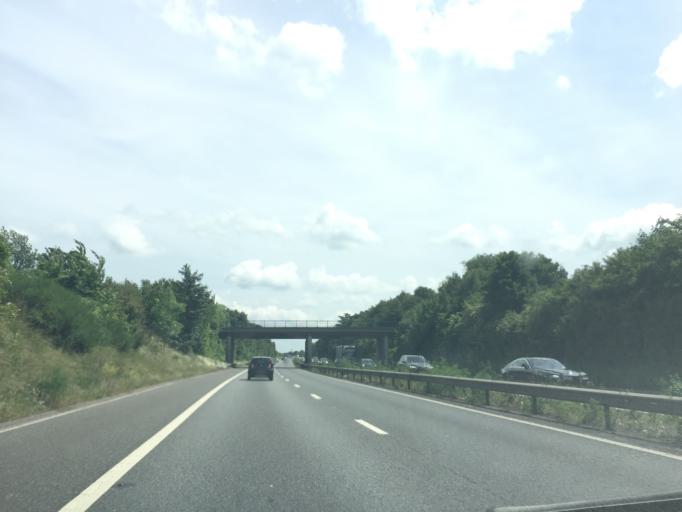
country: GB
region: England
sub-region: Kent
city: Sittingbourne
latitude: 51.3172
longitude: 0.6977
